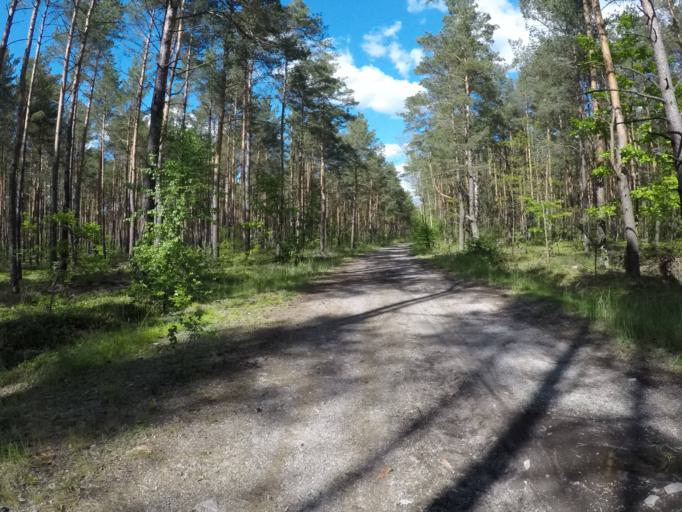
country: PL
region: Swietokrzyskie
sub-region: Powiat kielecki
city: Kostomloty Drugie
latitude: 50.8907
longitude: 20.5393
